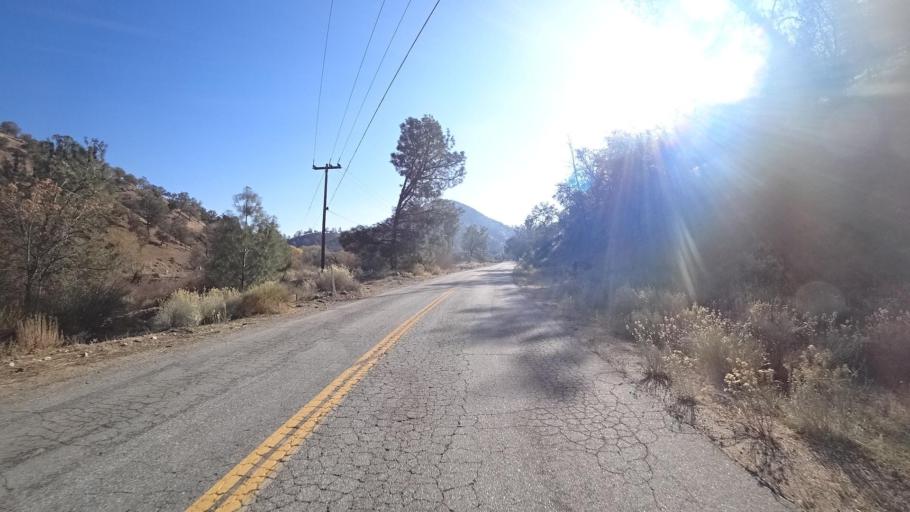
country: US
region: California
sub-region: Kern County
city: Golden Hills
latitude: 35.3063
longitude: -118.4417
